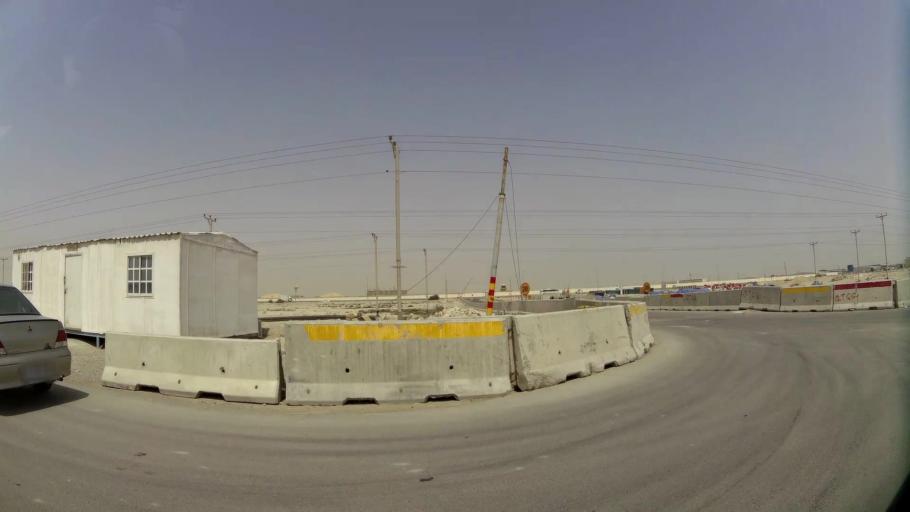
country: QA
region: Baladiyat ar Rayyan
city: Ar Rayyan
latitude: 25.1799
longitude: 51.4201
